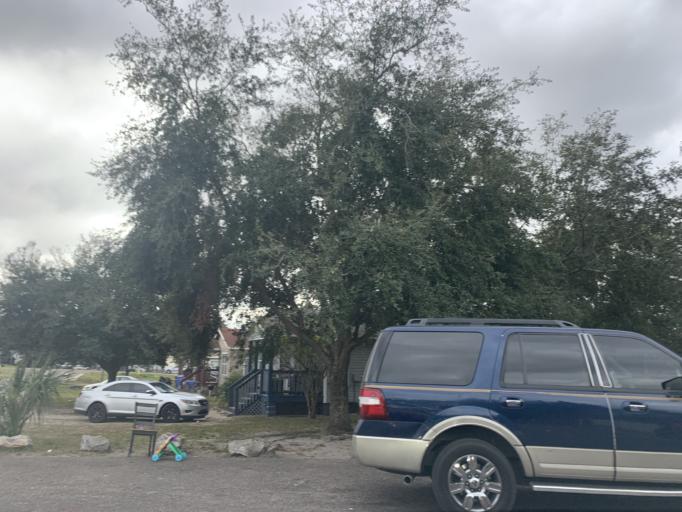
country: US
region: Florida
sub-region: Hillsborough County
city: East Lake-Orient Park
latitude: 27.9804
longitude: -82.3903
